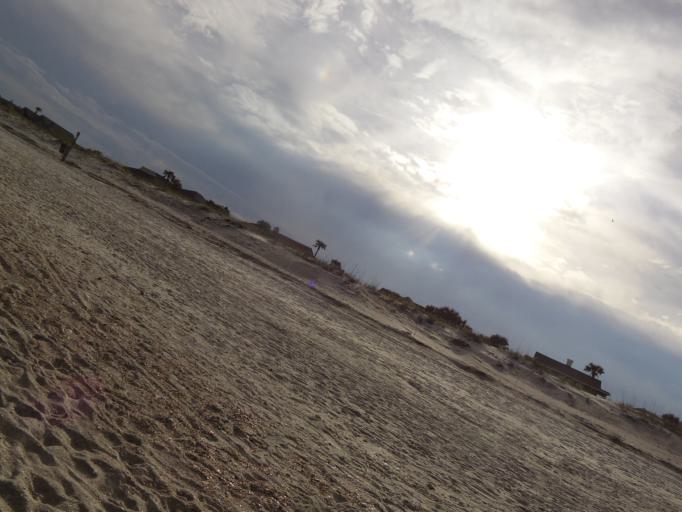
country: US
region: Florida
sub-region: Duval County
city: Neptune Beach
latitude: 30.3209
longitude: -81.3937
